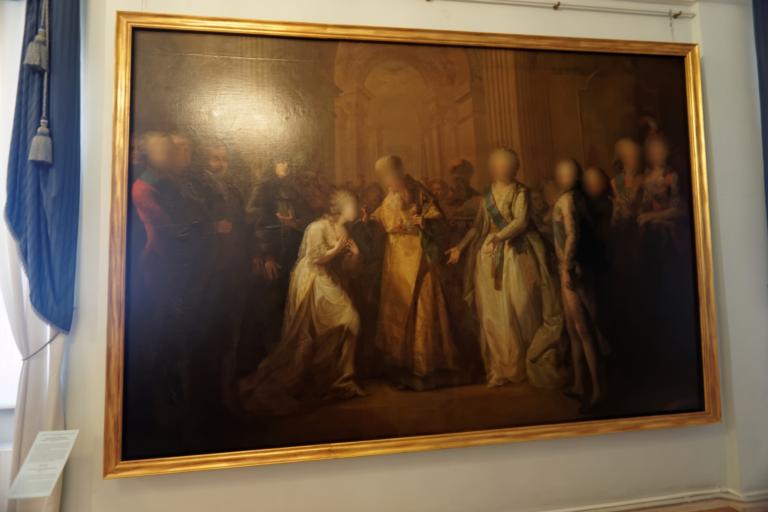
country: RU
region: St.-Petersburg
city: Saint Petersburg
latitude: 59.9402
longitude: 30.3371
